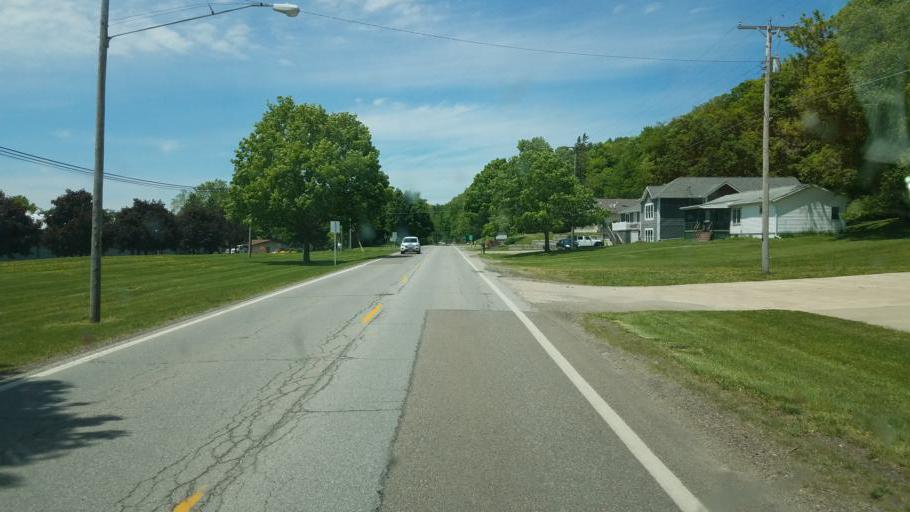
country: US
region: Ohio
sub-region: Sandusky County
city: Bellville
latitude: 40.6197
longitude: -82.5025
